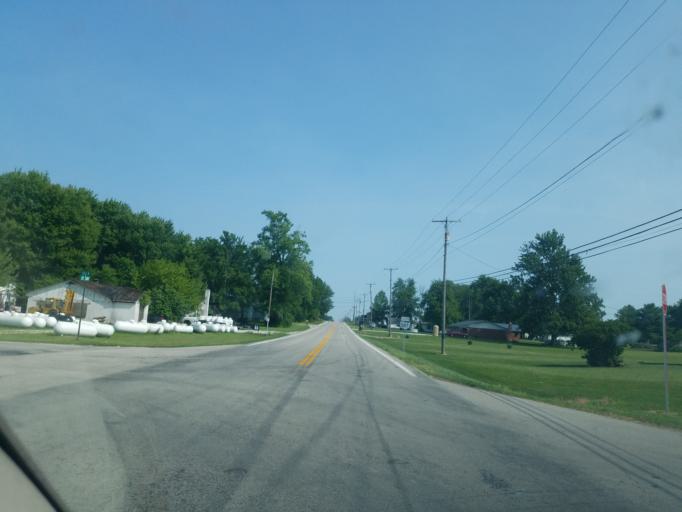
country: US
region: Ohio
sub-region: Wyandot County
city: Carey
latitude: 41.0289
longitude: -83.2982
